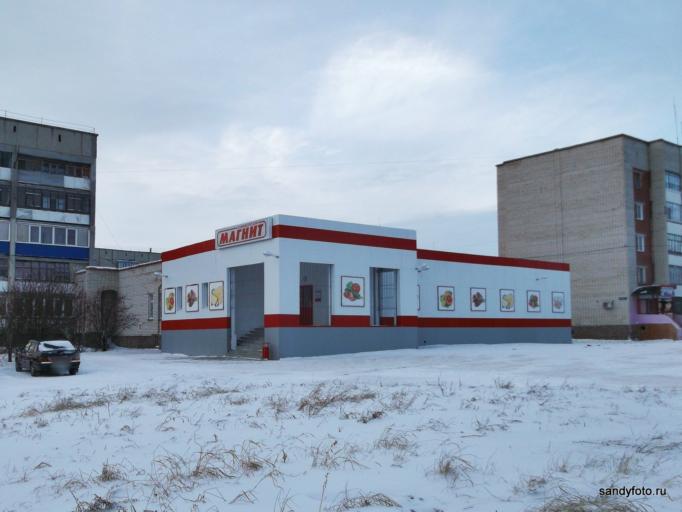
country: RU
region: Chelyabinsk
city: Troitsk
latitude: 54.0734
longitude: 61.5343
